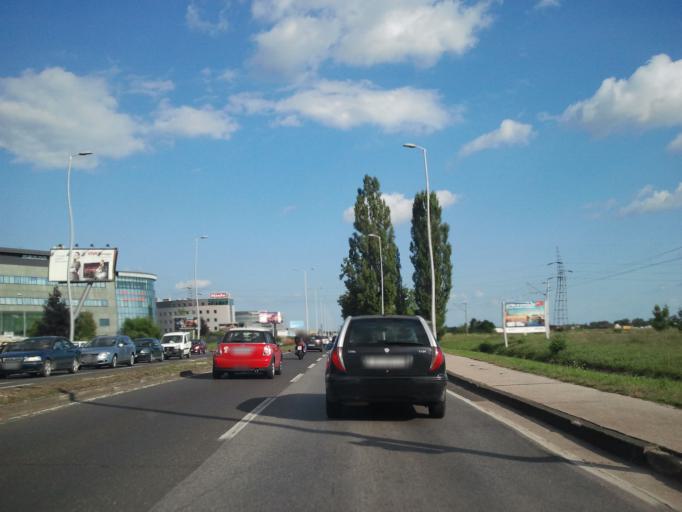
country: HR
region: Grad Zagreb
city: Odra
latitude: 45.7478
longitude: 15.9929
